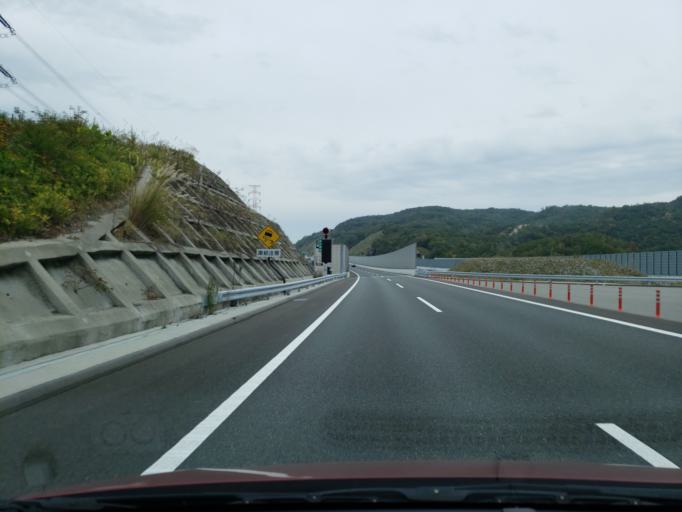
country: JP
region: Hyogo
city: Sandacho
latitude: 34.8560
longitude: 135.2469
